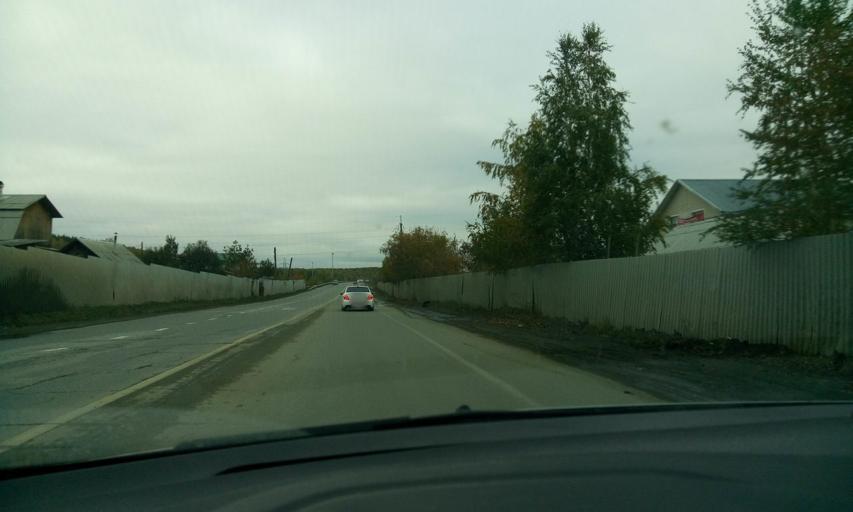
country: RU
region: Sverdlovsk
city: Istok
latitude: 56.7623
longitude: 60.7378
